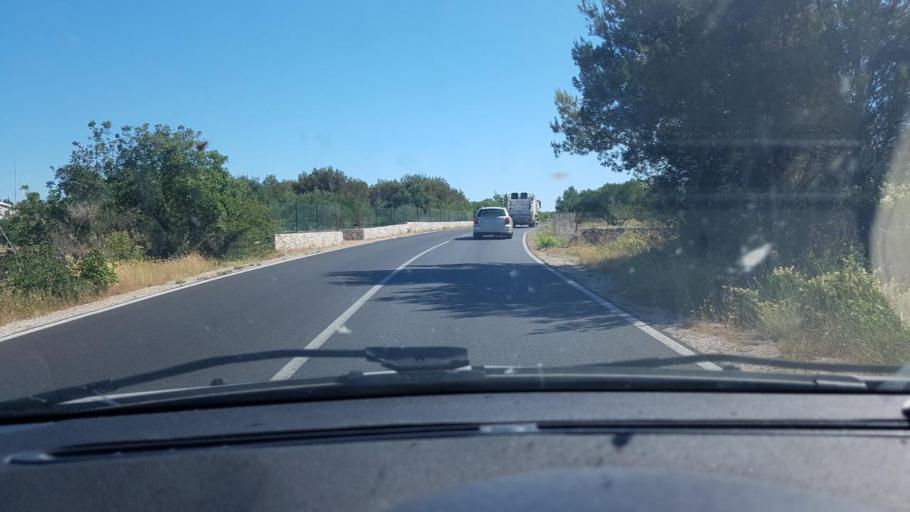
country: HR
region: Sibensko-Kniniska
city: Vodice
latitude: 43.7485
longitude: 15.8113
